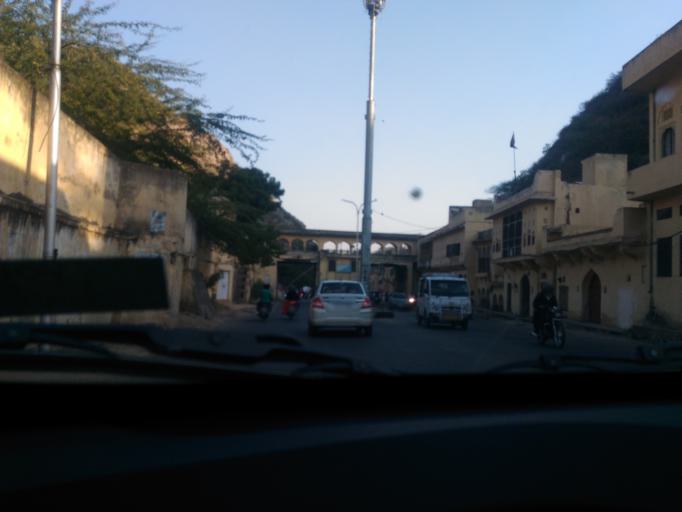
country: IN
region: Rajasthan
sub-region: Jaipur
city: Jaipur
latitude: 26.9021
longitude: 75.8515
